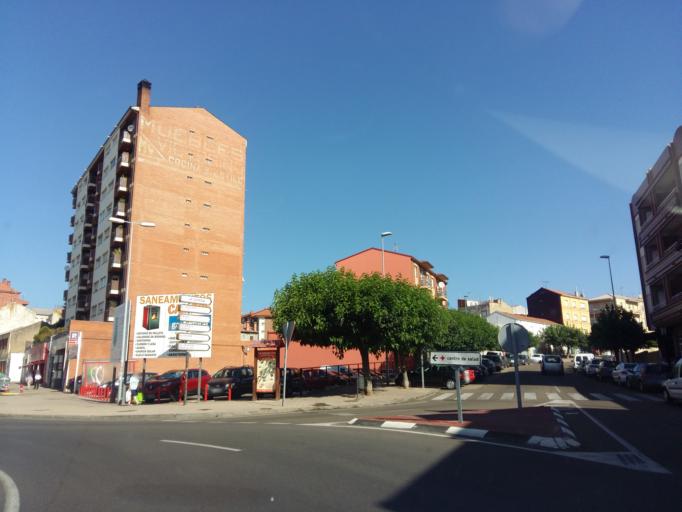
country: ES
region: Castille and Leon
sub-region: Provincia de Leon
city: Astorga
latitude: 42.4579
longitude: -6.0533
